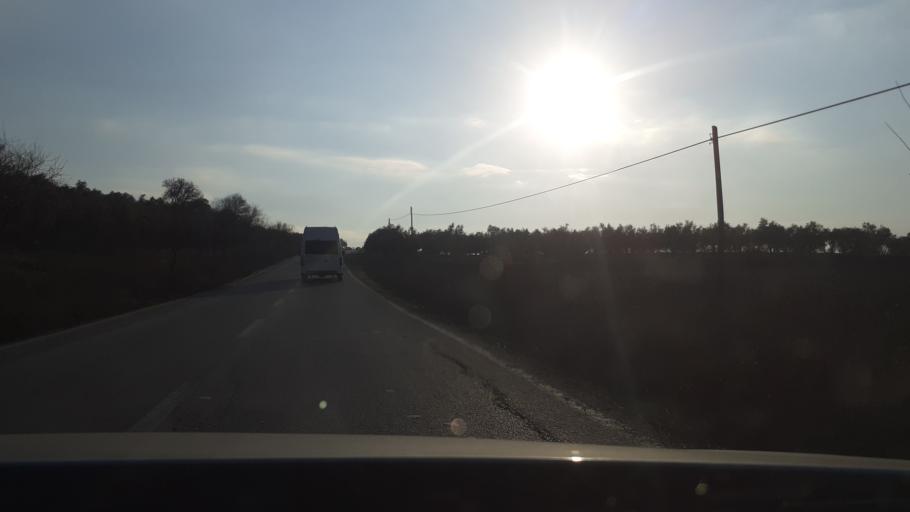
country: TR
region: Hatay
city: Oymakli
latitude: 36.1240
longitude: 36.3084
